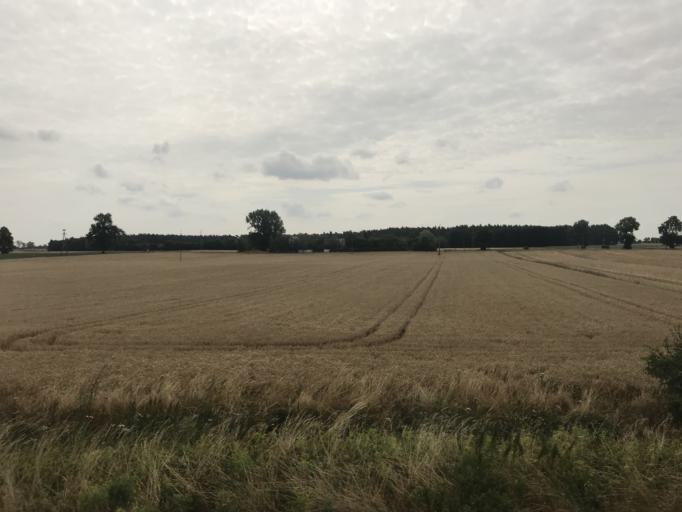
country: PL
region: Kujawsko-Pomorskie
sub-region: Powiat mogilenski
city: Mogilno
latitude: 52.6943
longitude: 18.0008
